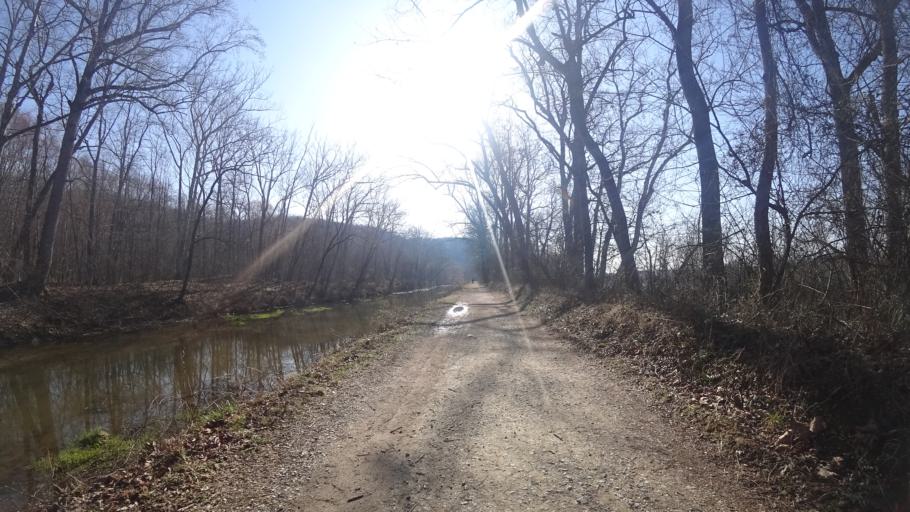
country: US
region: Virginia
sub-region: Loudoun County
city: Lowes Island
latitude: 39.0655
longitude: -77.3240
